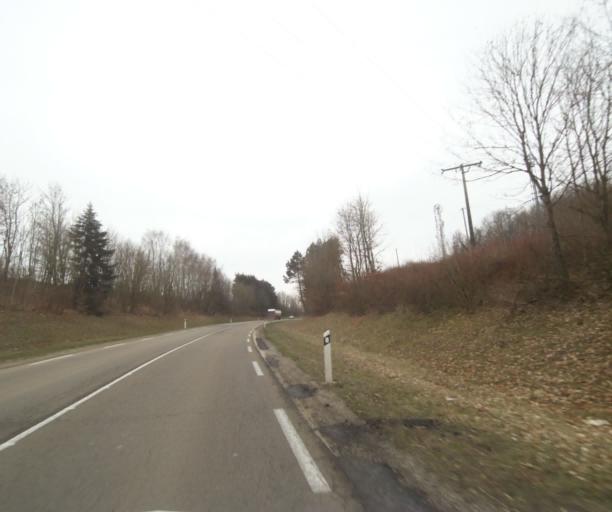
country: FR
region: Champagne-Ardenne
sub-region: Departement de la Haute-Marne
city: Bienville
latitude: 48.5774
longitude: 5.0346
